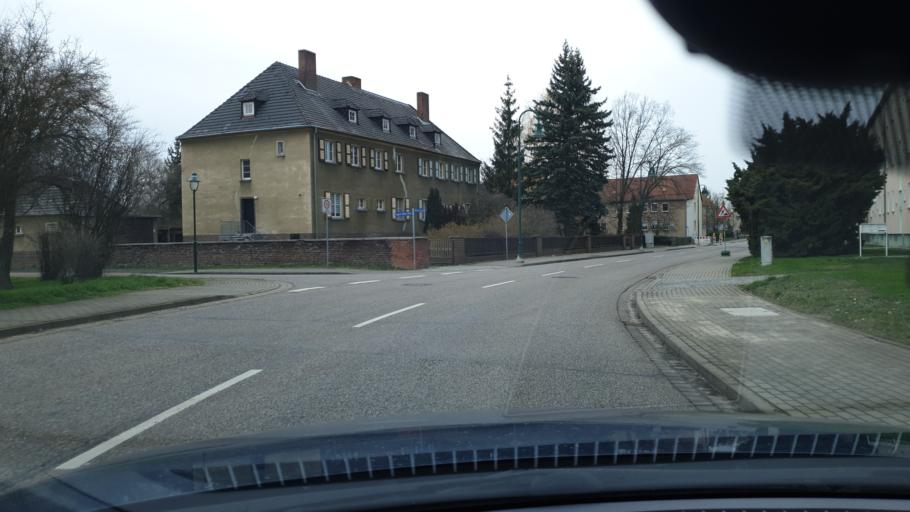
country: DE
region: Saxony-Anhalt
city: Vockerode
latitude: 51.8438
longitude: 12.3538
